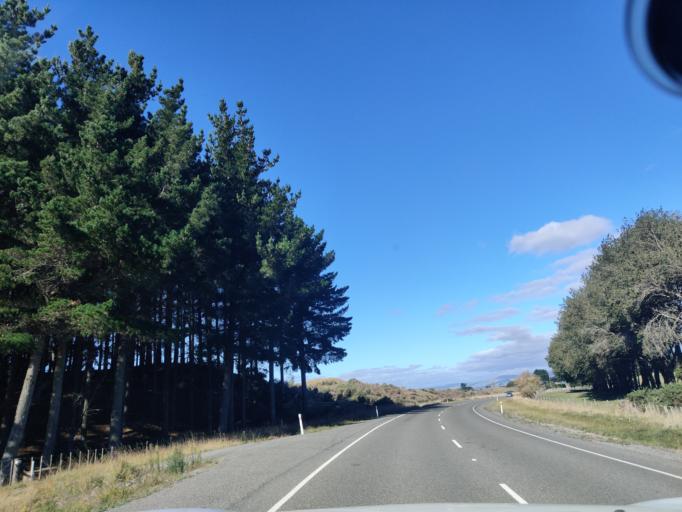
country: NZ
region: Manawatu-Wanganui
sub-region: Horowhenua District
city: Foxton
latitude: -40.4182
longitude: 175.4236
